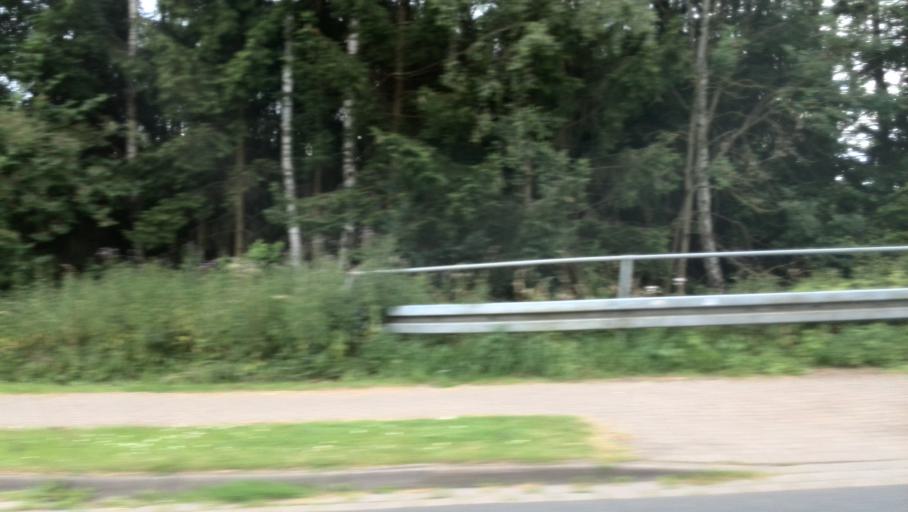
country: DE
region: Lower Saxony
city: Holle
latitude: 52.0961
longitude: 10.1485
